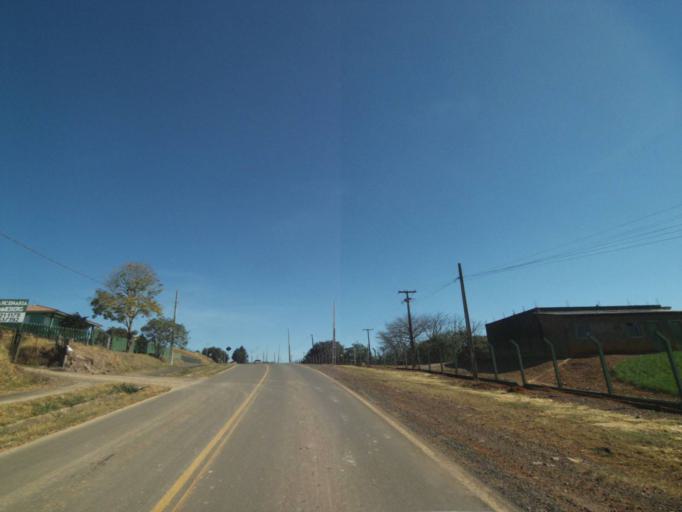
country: BR
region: Parana
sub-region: Tibagi
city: Tibagi
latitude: -24.5214
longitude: -50.4279
